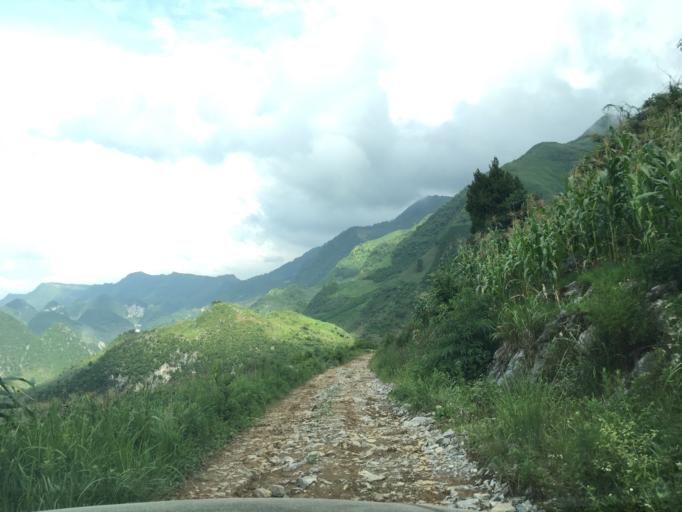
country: CN
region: Guangxi Zhuangzu Zizhiqu
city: Xinzhou
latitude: 24.9916
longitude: 105.6365
